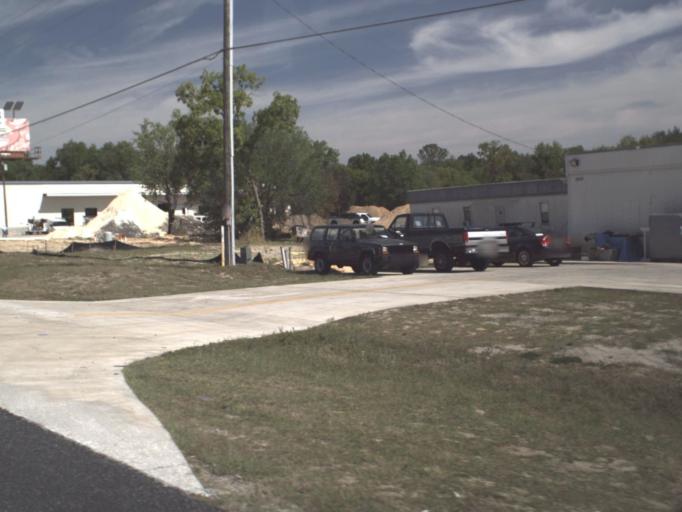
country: US
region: Florida
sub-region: Sumter County
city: The Villages
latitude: 29.0020
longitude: -82.0019
